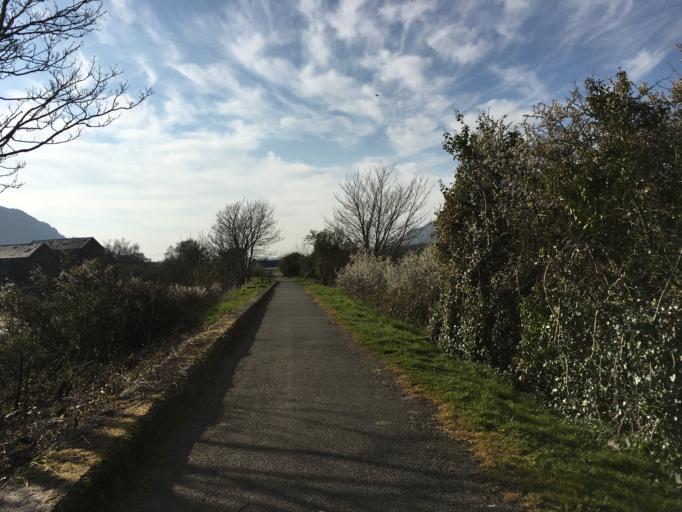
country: GB
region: Wales
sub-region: Gwynedd
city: Porthmadog
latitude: 52.9289
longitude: -4.1253
